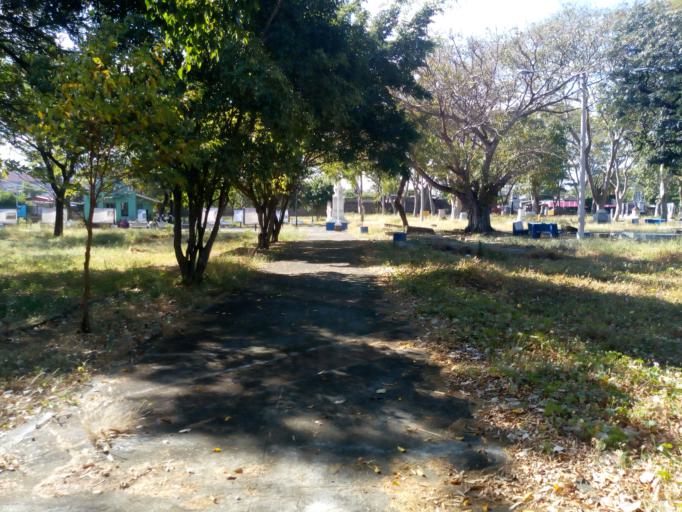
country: NI
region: Managua
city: Managua
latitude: 12.1479
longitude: -86.2758
